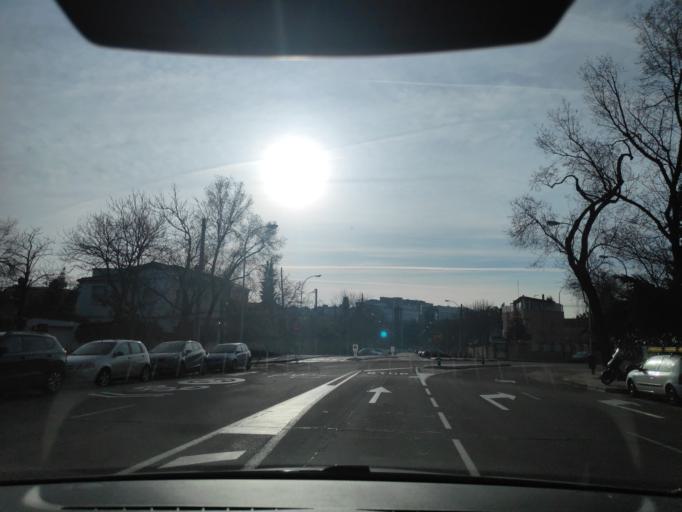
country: ES
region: Madrid
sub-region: Provincia de Madrid
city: Chamartin
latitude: 40.4583
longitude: -3.6673
